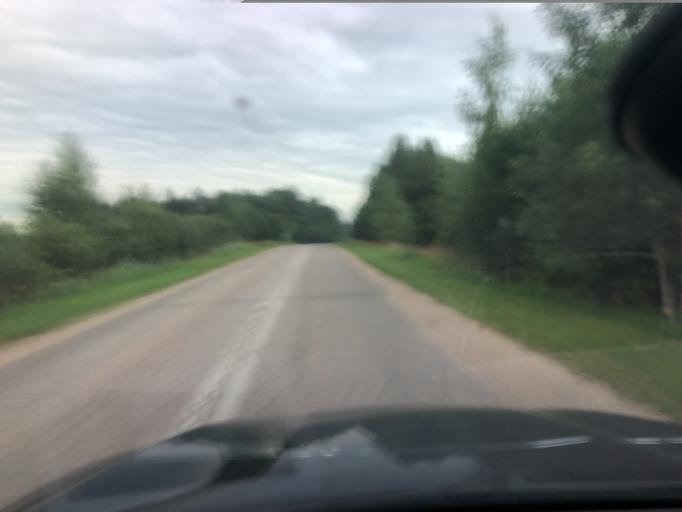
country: RU
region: Jaroslavl
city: Pereslavl'-Zalesskiy
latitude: 57.0124
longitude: 38.9655
